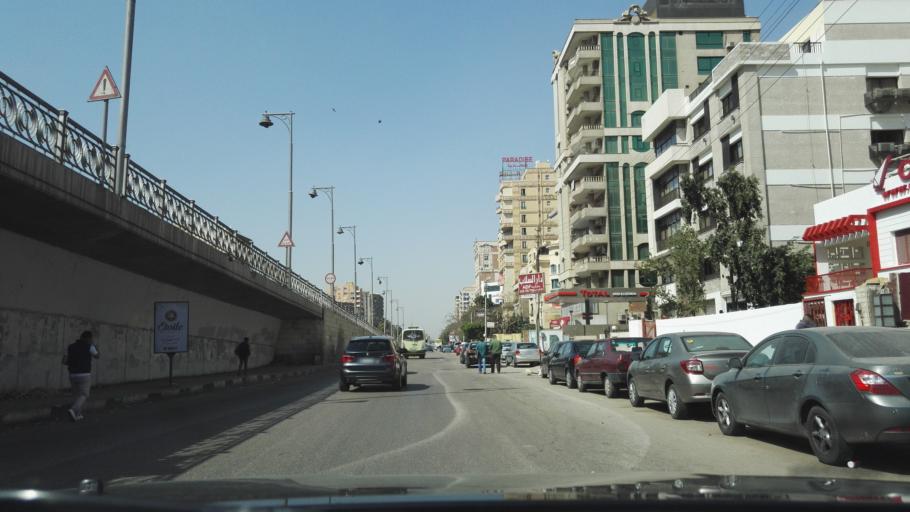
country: EG
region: Muhafazat al Qahirah
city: Cairo
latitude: 30.0846
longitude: 31.3408
